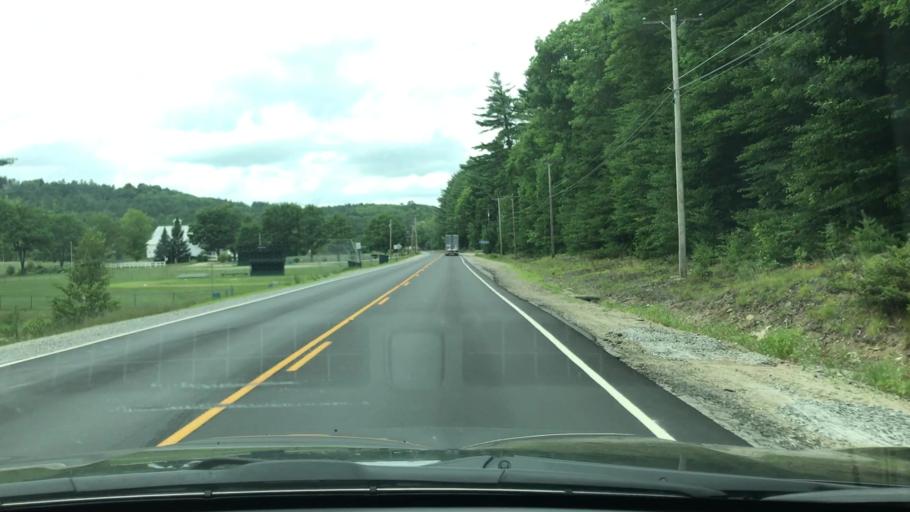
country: US
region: Maine
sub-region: Oxford County
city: West Paris
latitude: 44.3834
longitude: -70.6527
